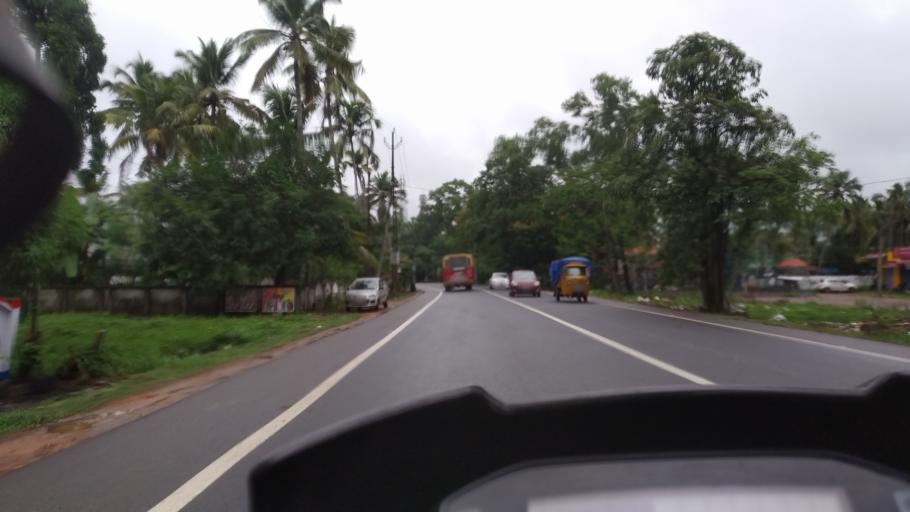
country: IN
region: Kerala
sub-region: Alappuzha
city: Mavelikara
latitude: 9.2868
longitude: 76.4391
